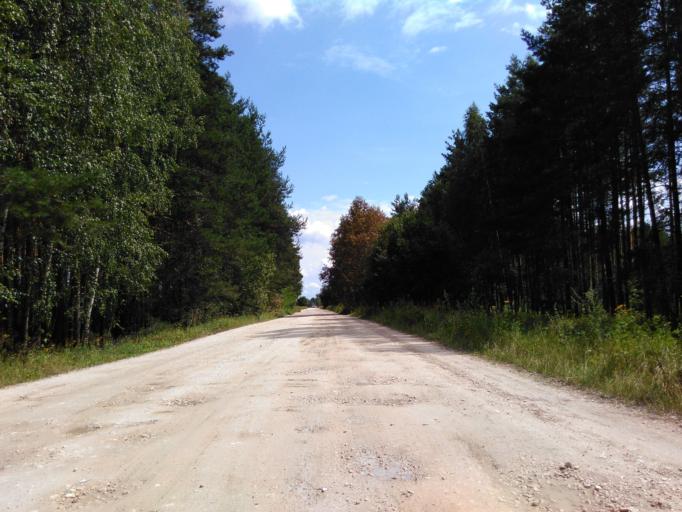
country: RU
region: Vladimir
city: Krasnyy Oktyabr'
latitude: 56.0037
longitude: 38.8405
